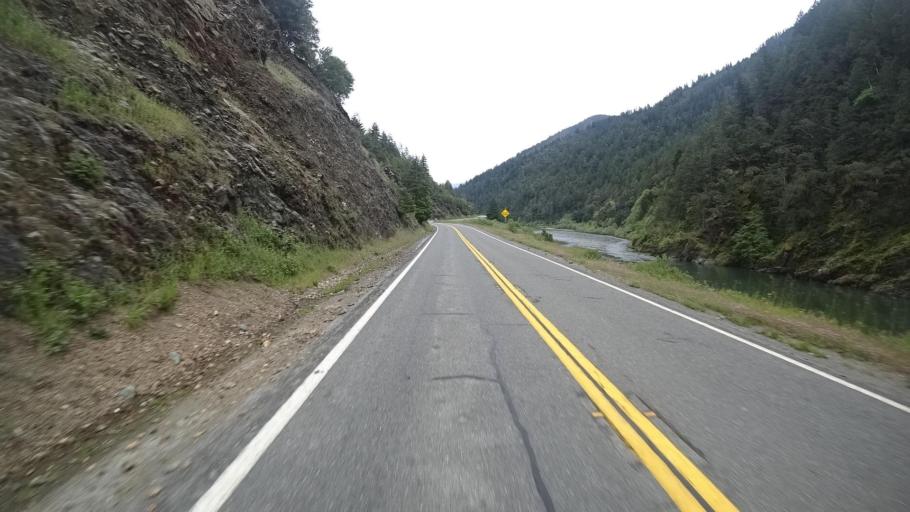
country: US
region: California
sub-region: Humboldt County
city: Willow Creek
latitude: 41.2502
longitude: -123.6457
